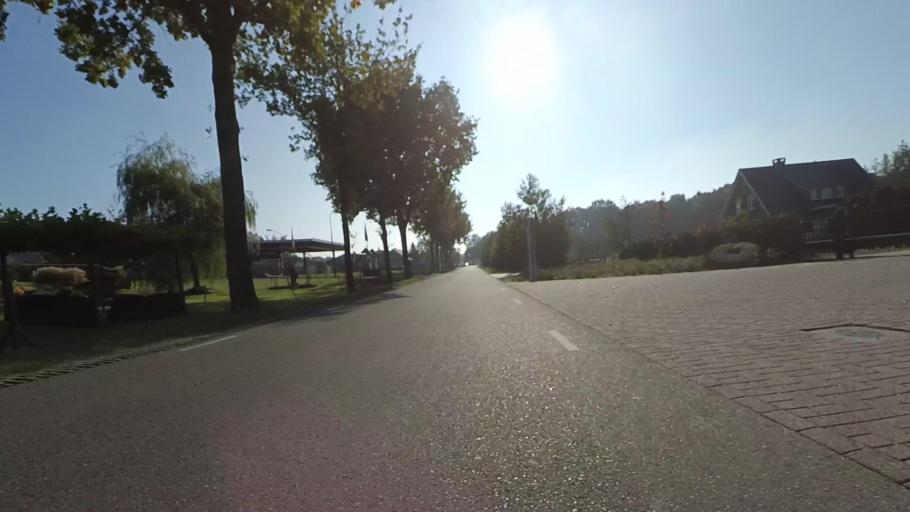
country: NL
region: Gelderland
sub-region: Gemeente Putten
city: Putten
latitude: 52.2496
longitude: 5.5494
